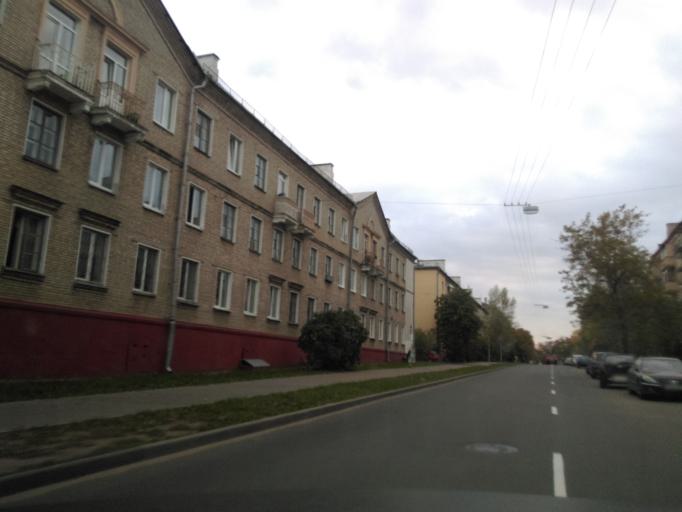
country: BY
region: Minsk
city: Minsk
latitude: 53.9125
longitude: 27.5853
